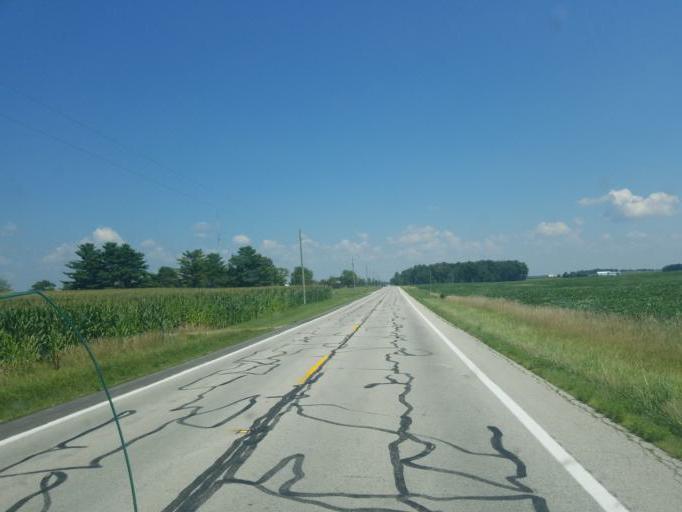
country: US
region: Ohio
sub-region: Shelby County
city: Jackson Center
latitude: 40.3959
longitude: -84.0816
